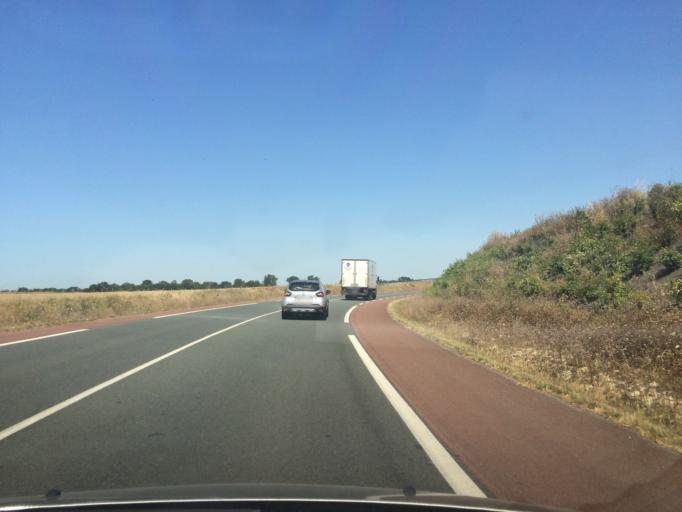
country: FR
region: Poitou-Charentes
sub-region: Departement de la Charente-Maritime
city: Saint-Xandre
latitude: 46.2359
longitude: -1.0766
